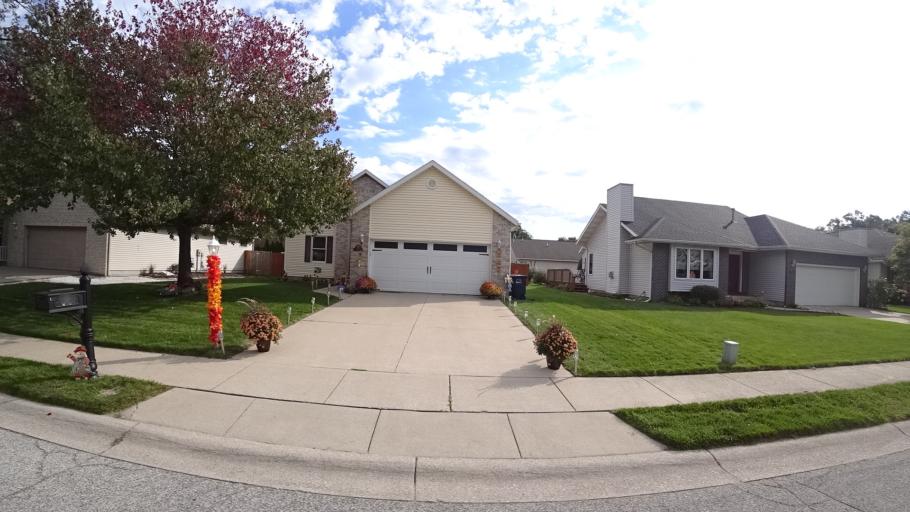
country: US
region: Indiana
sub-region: LaPorte County
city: Trail Creek
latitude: 41.6996
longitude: -86.8666
